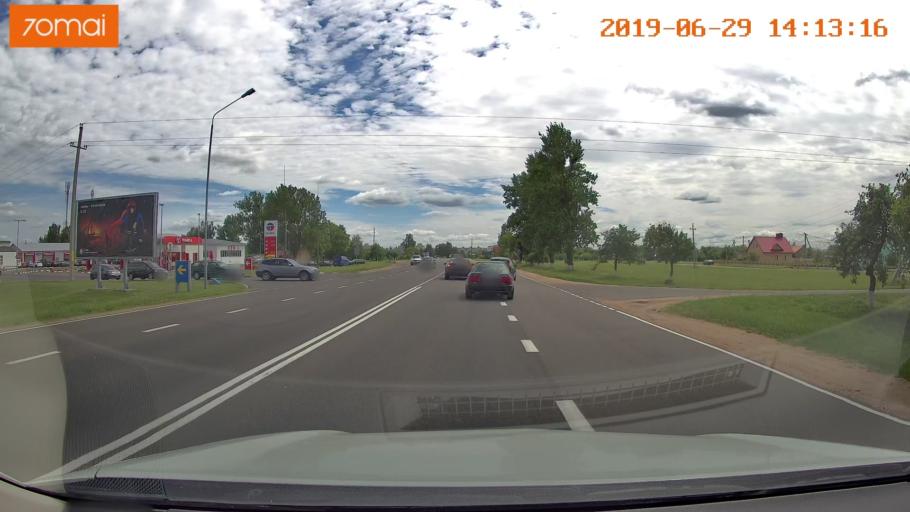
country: BY
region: Minsk
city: Salihorsk
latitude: 52.8040
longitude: 27.5102
